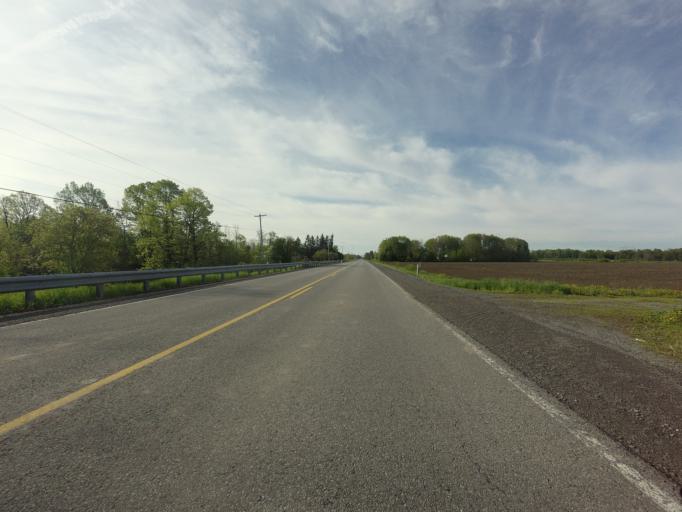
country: CA
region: Ontario
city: Ottawa
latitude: 45.2801
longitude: -75.4430
